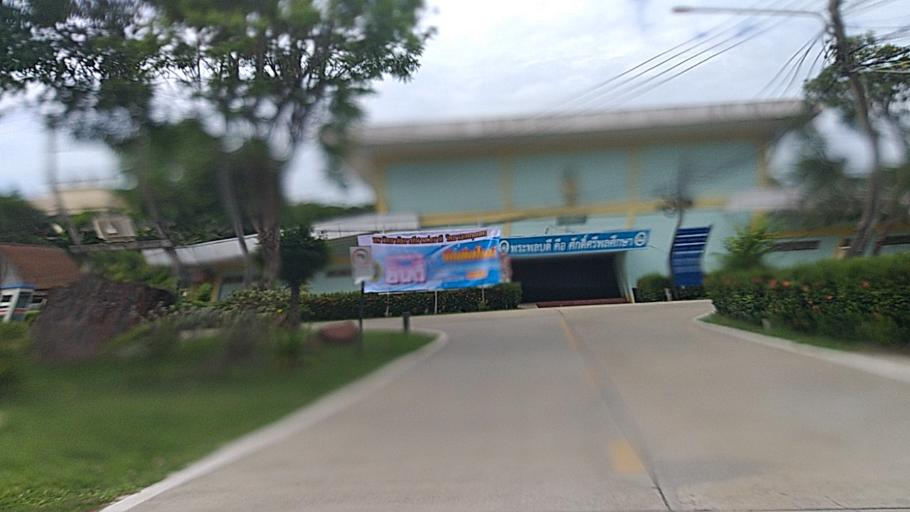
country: TH
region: Pathum Thani
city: Nong Suea
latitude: 14.0721
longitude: 100.8868
